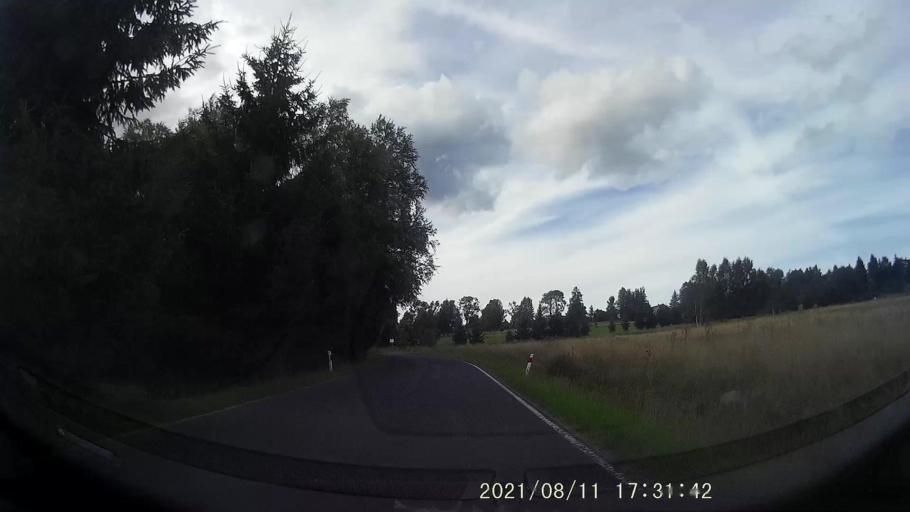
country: PL
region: Lower Silesian Voivodeship
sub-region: Powiat klodzki
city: Szczytna
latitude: 50.3028
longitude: 16.4545
